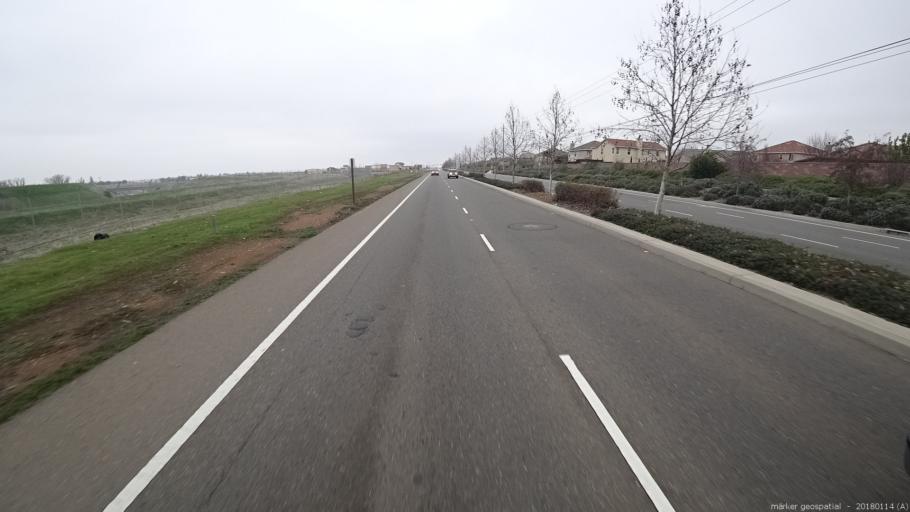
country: US
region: California
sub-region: Sacramento County
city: Rancho Cordova
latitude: 38.5523
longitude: -121.2430
